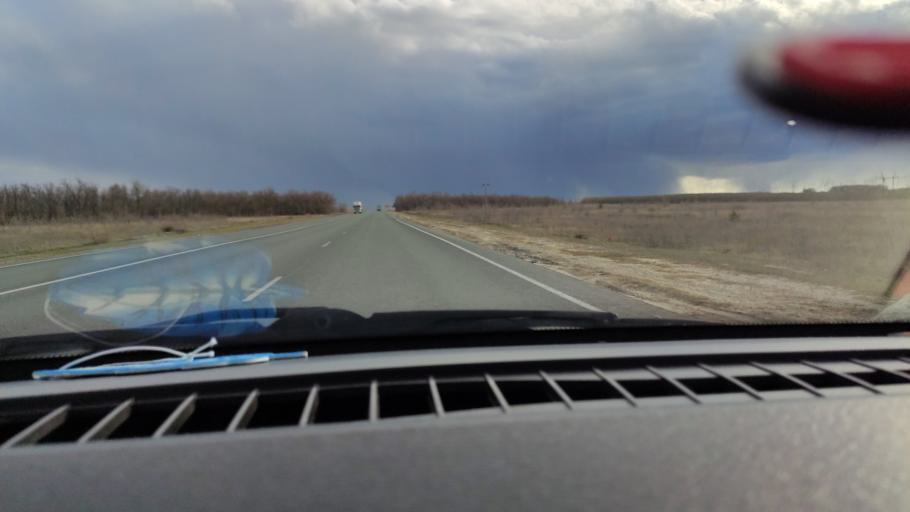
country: RU
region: Saratov
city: Sinodskoye
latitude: 51.9105
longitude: 46.5528
